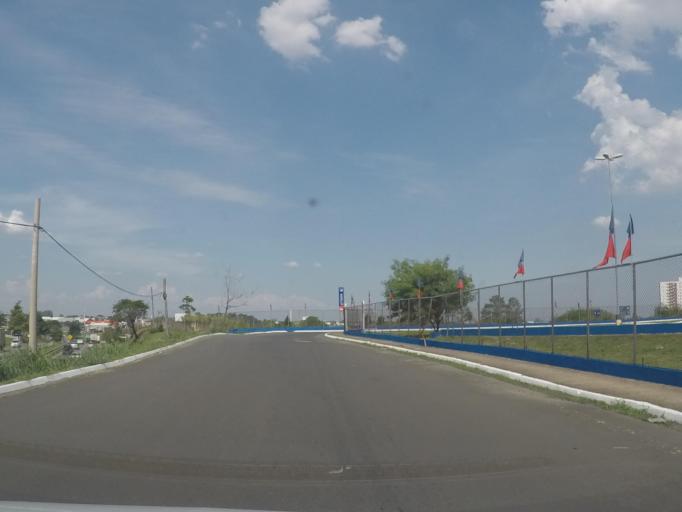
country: BR
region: Sao Paulo
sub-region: Sumare
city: Sumare
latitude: -22.8072
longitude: -47.2481
